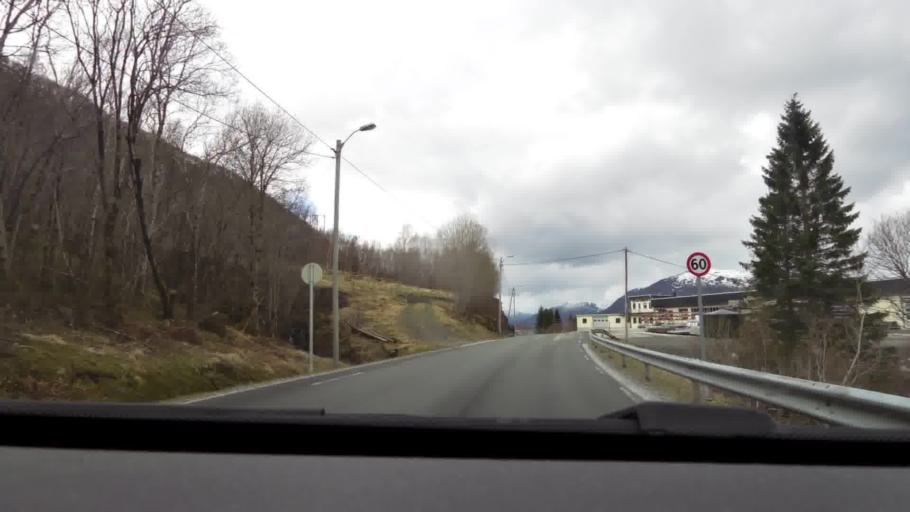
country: NO
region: More og Romsdal
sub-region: Eide
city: Eide
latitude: 62.9061
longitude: 7.5211
